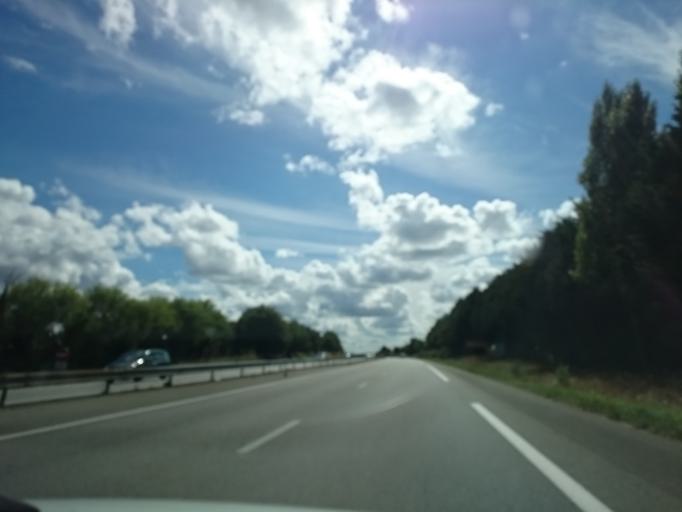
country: FR
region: Pays de la Loire
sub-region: Departement de la Loire-Atlantique
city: Mauves-sur-Loire
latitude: 47.3268
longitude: -1.4040
